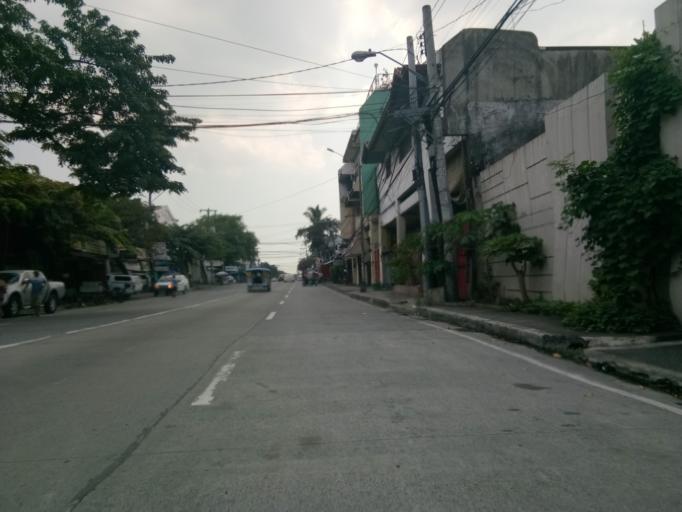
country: PH
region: Metro Manila
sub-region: Marikina
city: Calumpang
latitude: 14.6197
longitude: 121.0636
